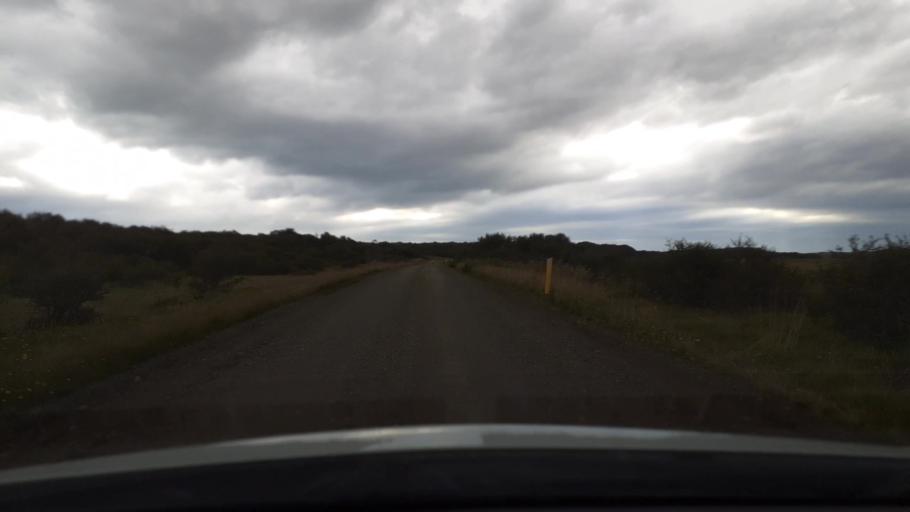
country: IS
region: West
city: Borgarnes
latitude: 64.6136
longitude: -21.9509
